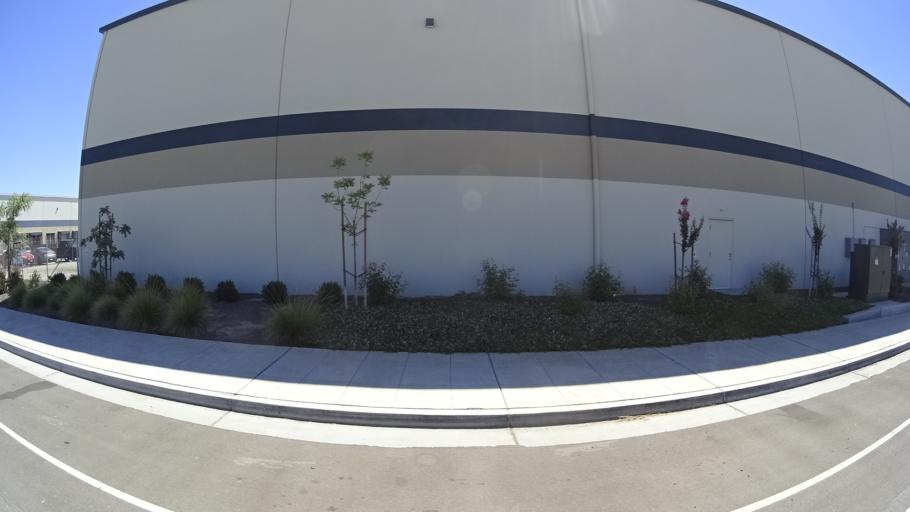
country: US
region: California
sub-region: Fresno County
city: Easton
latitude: 36.6864
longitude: -119.7727
